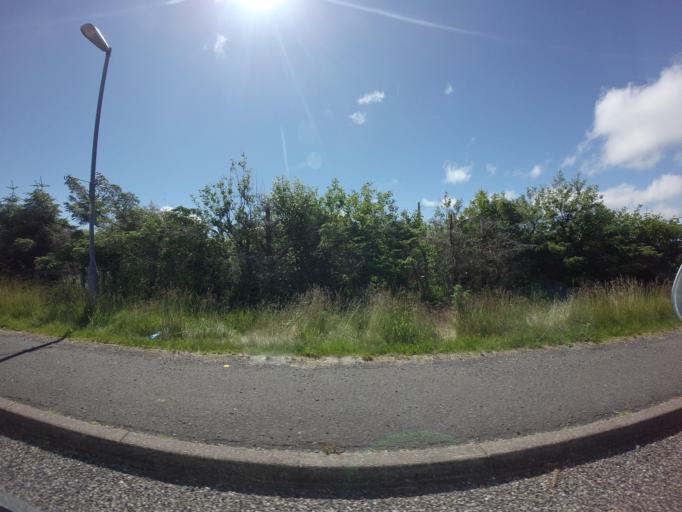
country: GB
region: Scotland
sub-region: Eilean Siar
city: Harris
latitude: 58.1908
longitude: -6.7076
